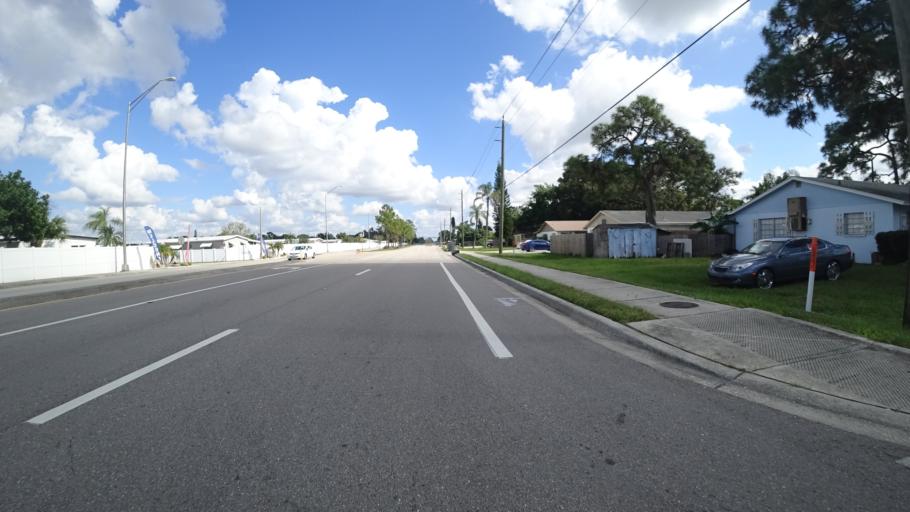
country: US
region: Florida
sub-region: Manatee County
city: Whitfield
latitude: 27.4293
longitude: -82.5710
